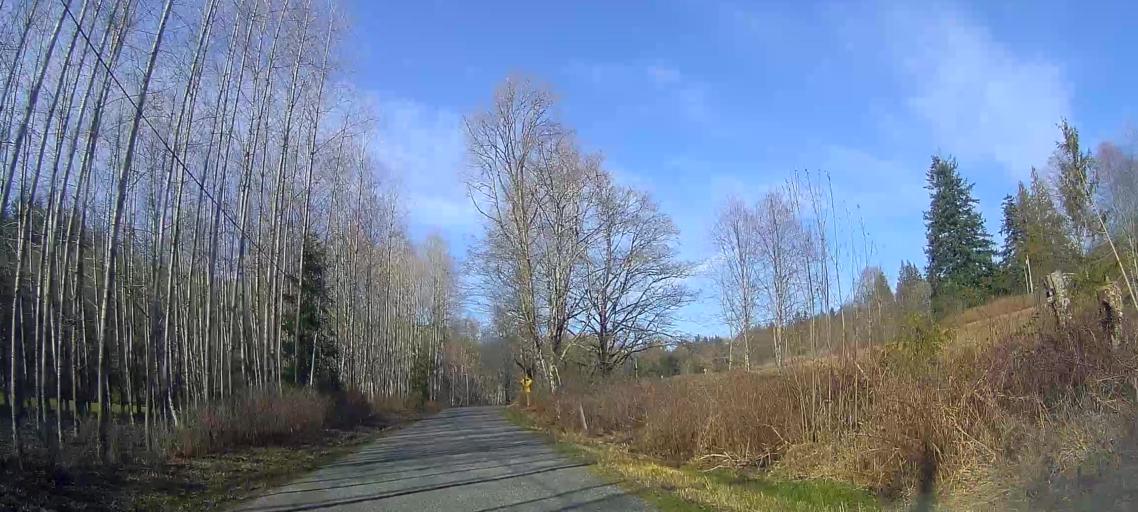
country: US
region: Washington
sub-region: Skagit County
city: Burlington
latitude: 48.5956
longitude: -122.3668
